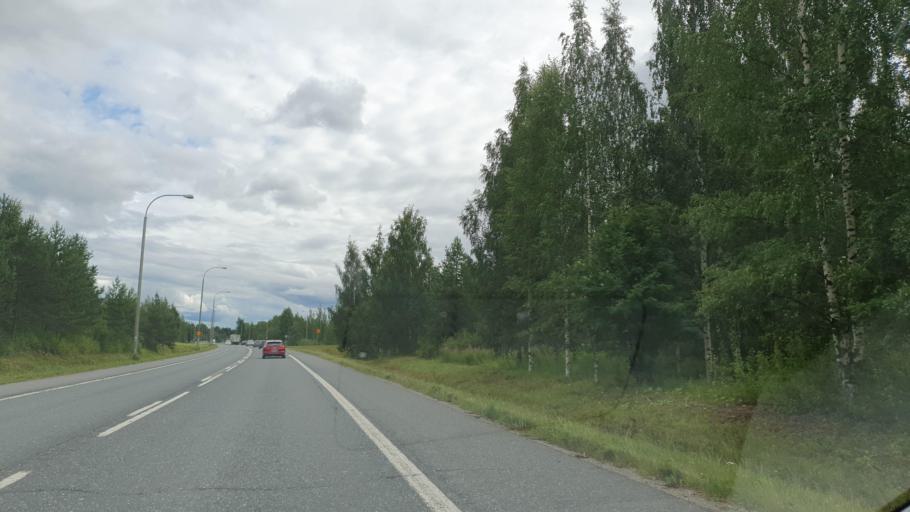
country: FI
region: Northern Savo
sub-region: Ylae-Savo
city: Iisalmi
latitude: 63.5746
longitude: 27.2400
